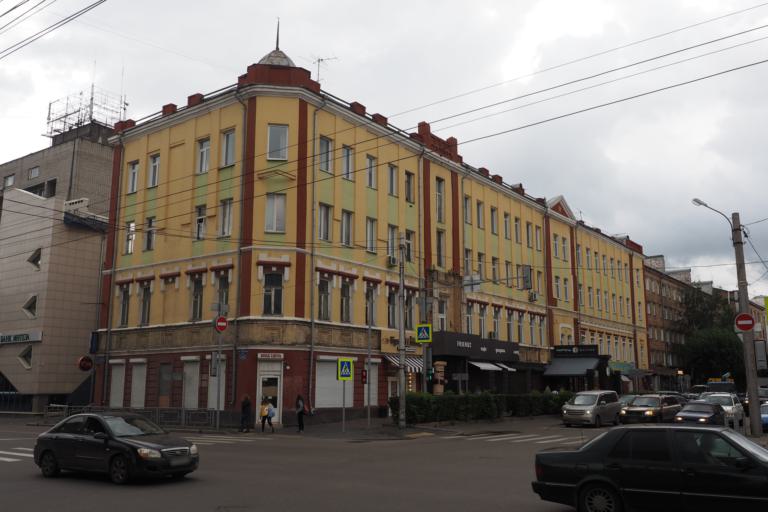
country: RU
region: Krasnoyarskiy
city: Krasnoyarsk
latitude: 56.0129
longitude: 92.8584
